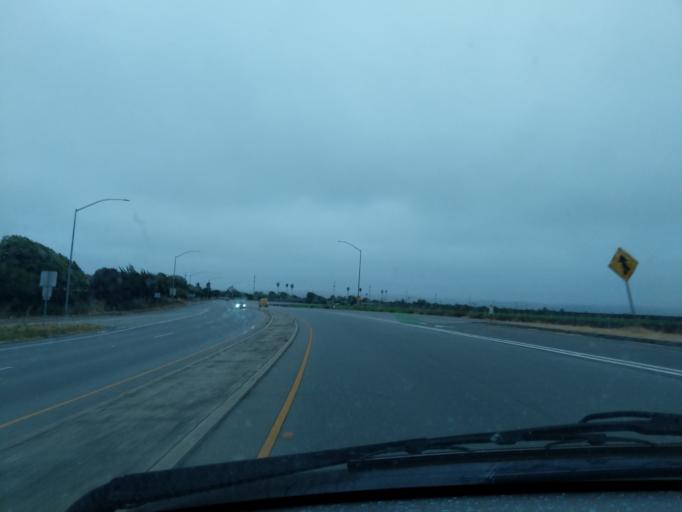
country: US
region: California
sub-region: Monterey County
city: Boronda
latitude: 36.6827
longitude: -121.6751
